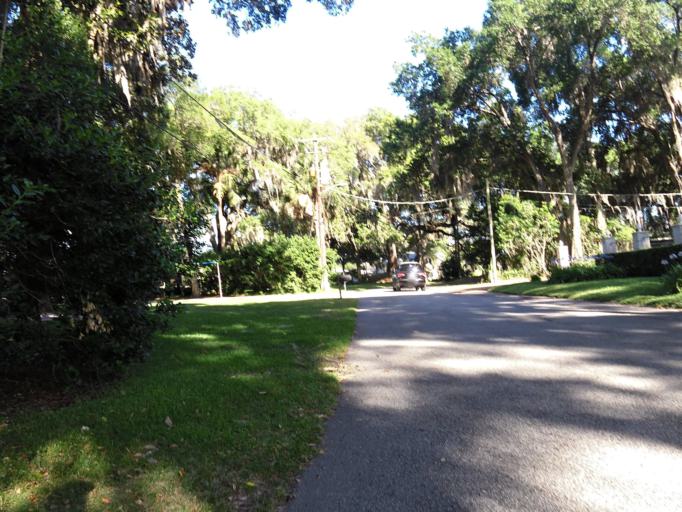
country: US
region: Florida
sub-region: Duval County
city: Jacksonville
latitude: 30.3150
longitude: -81.6136
